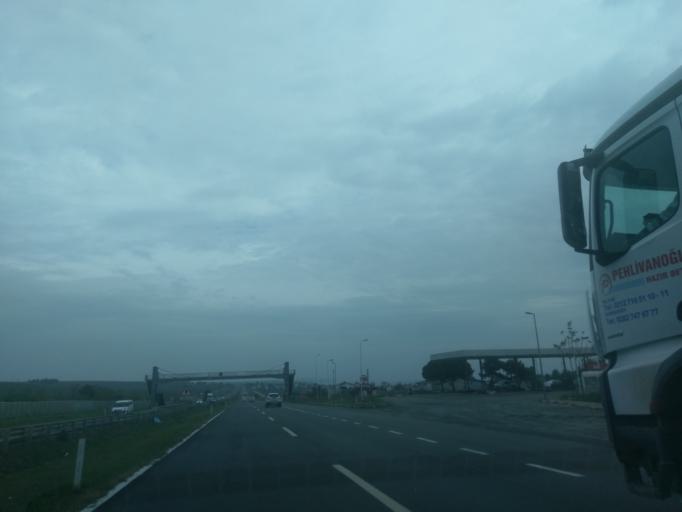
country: TR
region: Istanbul
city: Canta
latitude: 41.0760
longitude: 28.1440
